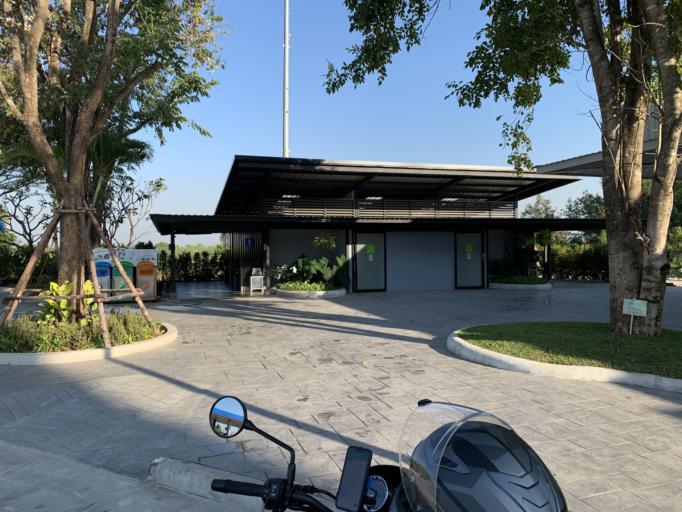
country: TH
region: Sukhothai
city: Sawankhalok
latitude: 17.3340
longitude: 99.8480
